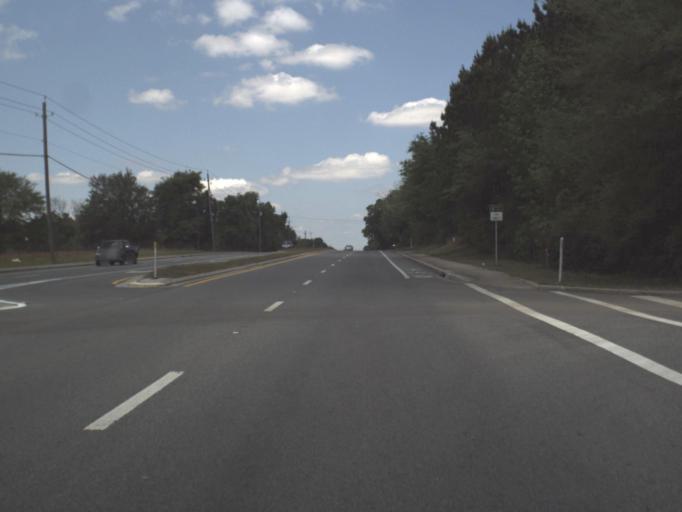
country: US
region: Florida
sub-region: Santa Rosa County
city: Point Baker
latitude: 30.6751
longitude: -87.0541
